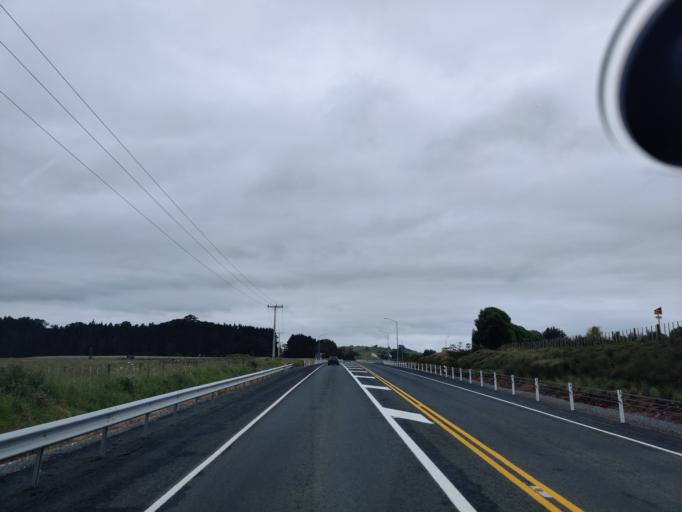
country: NZ
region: Northland
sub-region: Whangarei
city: Ruakaka
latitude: -36.1239
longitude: 174.1776
